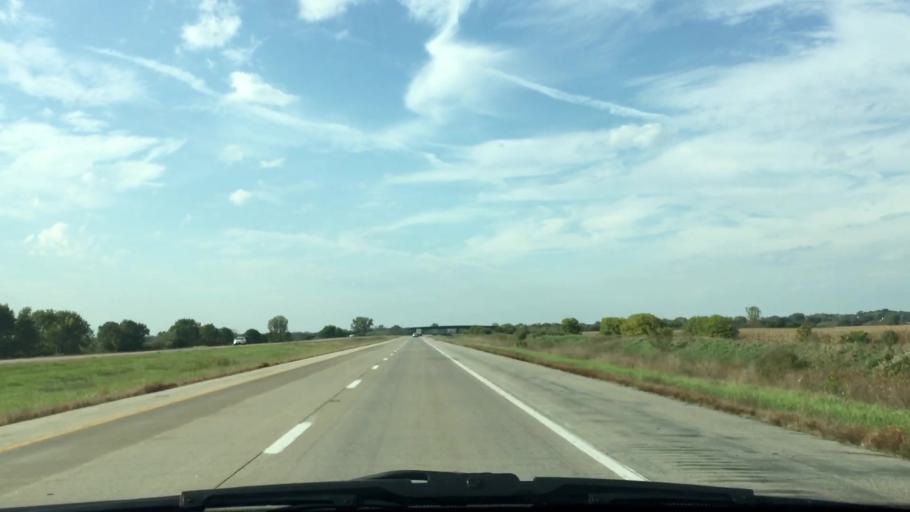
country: US
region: Illinois
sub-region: Whiteside County
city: Erie
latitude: 41.6493
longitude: -90.1570
